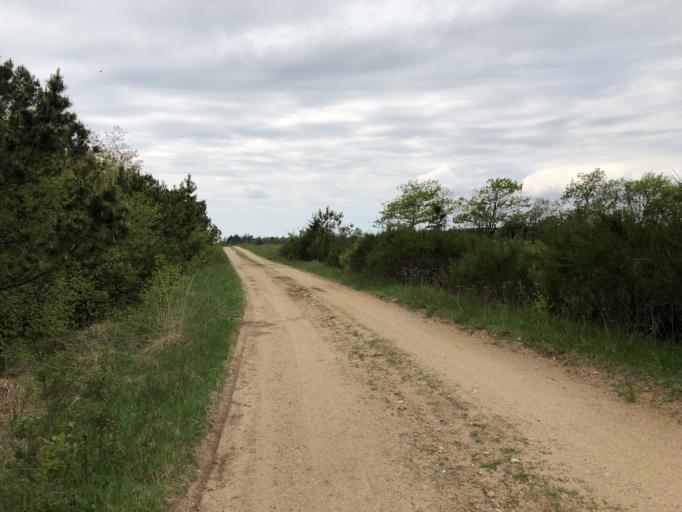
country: DK
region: Central Jutland
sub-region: Holstebro Kommune
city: Ulfborg
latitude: 56.2977
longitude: 8.4182
